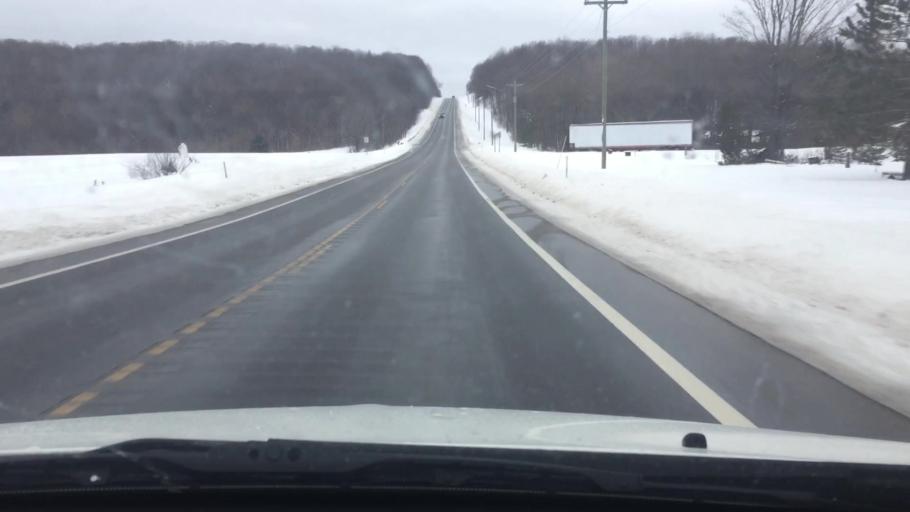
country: US
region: Michigan
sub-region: Charlevoix County
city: Boyne City
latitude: 45.0964
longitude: -85.0005
